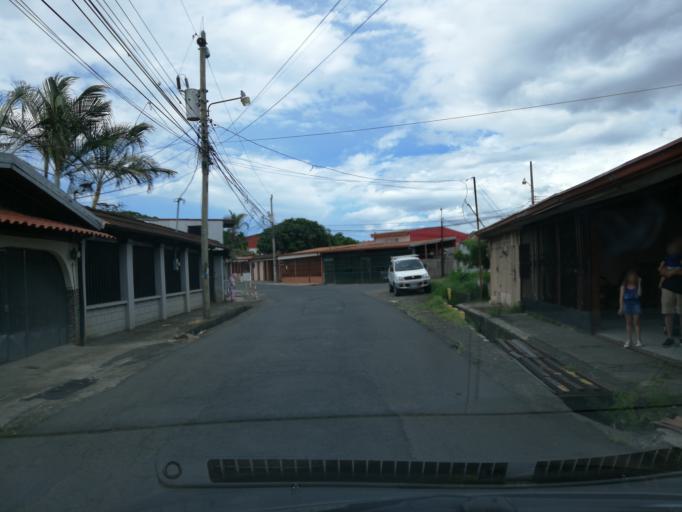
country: CR
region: Alajuela
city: Alajuela
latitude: 10.0011
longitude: -84.2159
